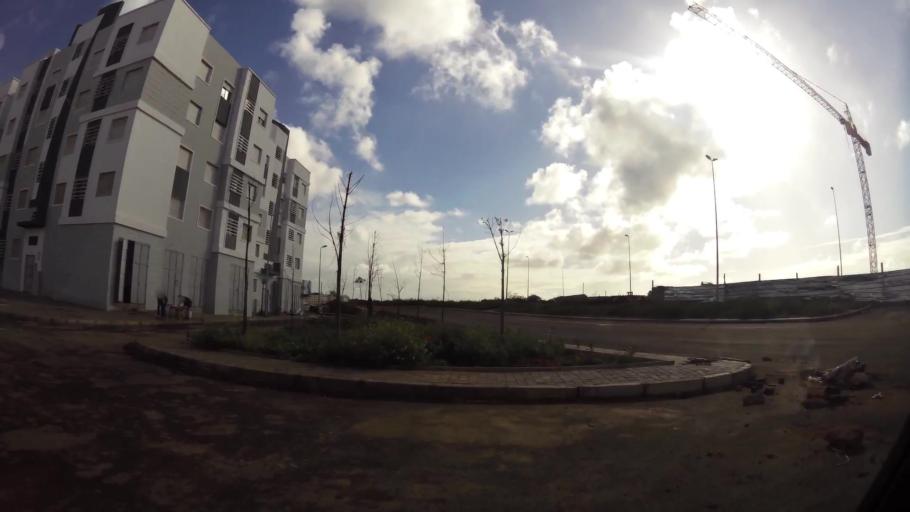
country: MA
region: Grand Casablanca
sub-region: Casablanca
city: Casablanca
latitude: 33.5544
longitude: -7.7060
